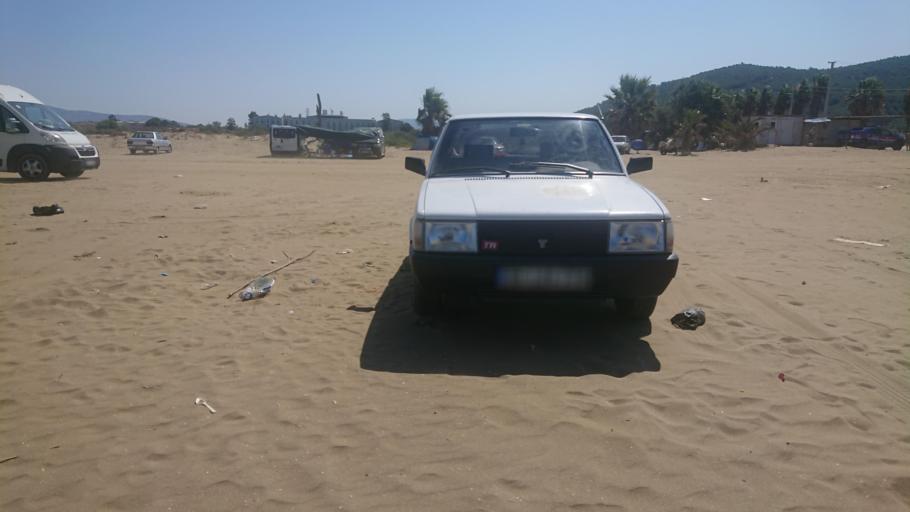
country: TR
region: Aydin
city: Kusadasi
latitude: 37.9440
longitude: 27.2738
